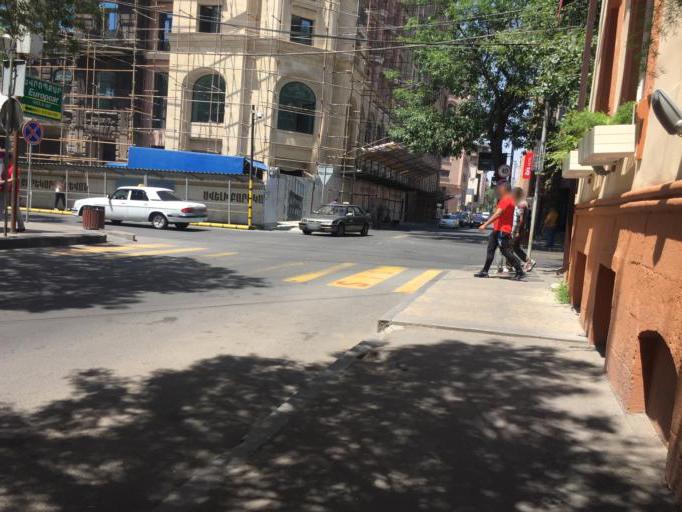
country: AM
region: Yerevan
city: Yerevan
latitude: 40.1806
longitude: 44.5156
